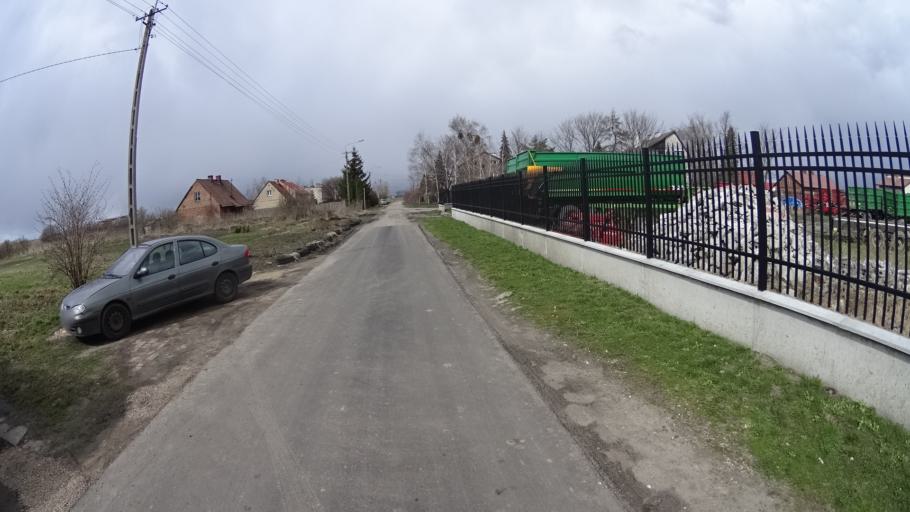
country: PL
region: Masovian Voivodeship
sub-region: Powiat warszawski zachodni
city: Jozefow
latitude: 52.2190
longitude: 20.6688
